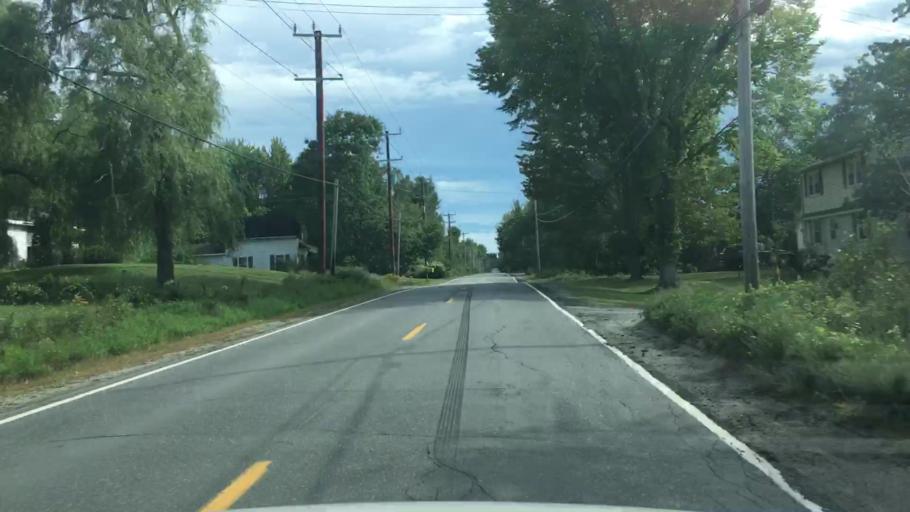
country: US
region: Maine
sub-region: Hancock County
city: Ellsworth
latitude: 44.4967
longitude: -68.4204
